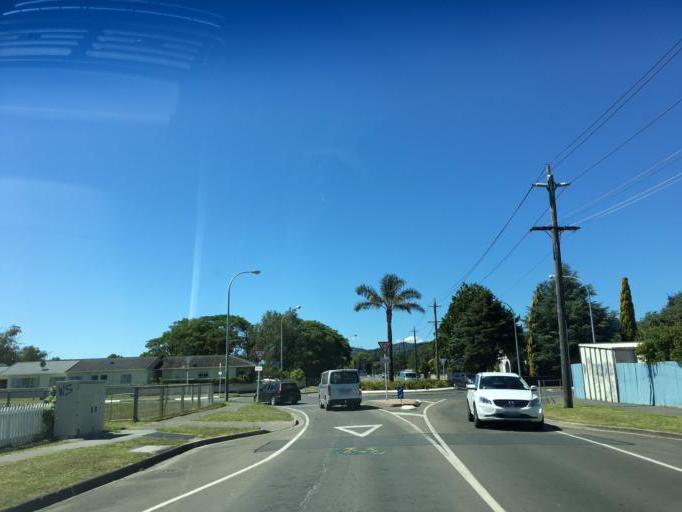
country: NZ
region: Gisborne
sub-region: Gisborne District
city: Gisborne
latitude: -38.6605
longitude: 178.0077
